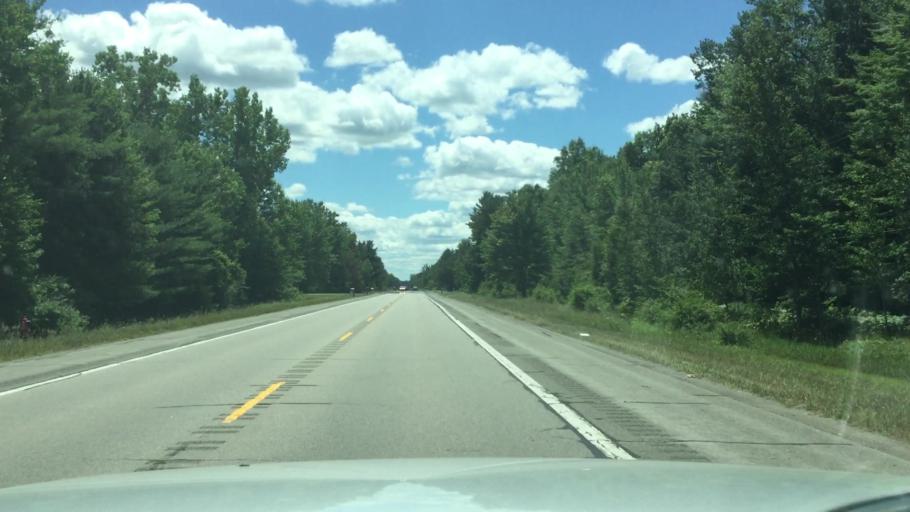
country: US
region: Michigan
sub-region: Saginaw County
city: Shields
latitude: 43.3915
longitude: -84.1312
